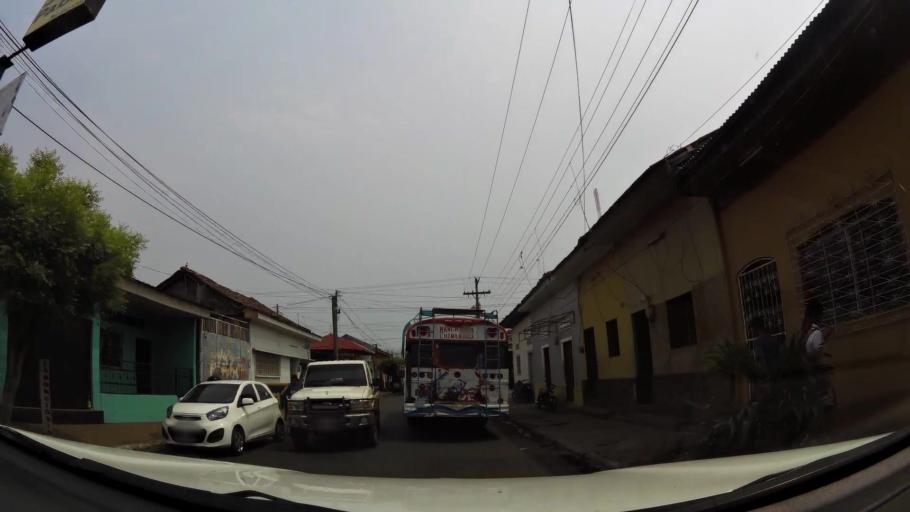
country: NI
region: Chinandega
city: Chinandega
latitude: 12.6338
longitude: -87.1321
